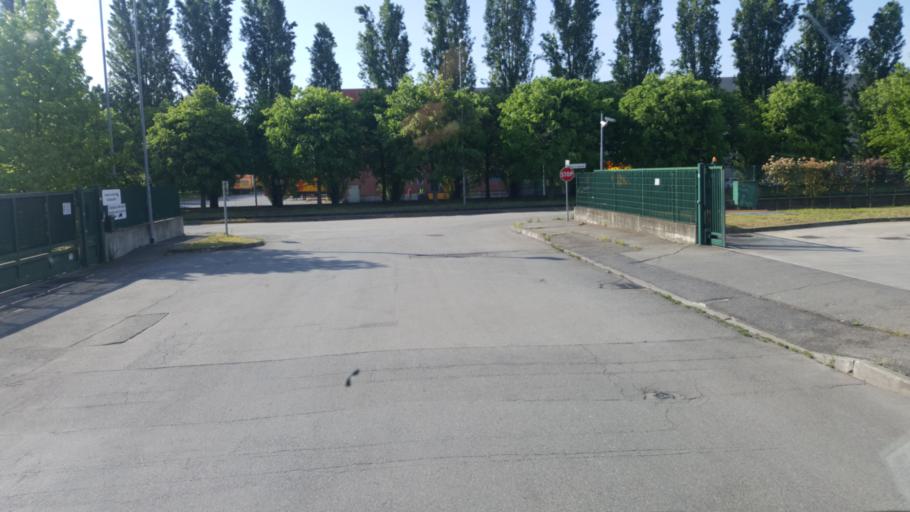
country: IT
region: Lombardy
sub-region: Citta metropolitana di Milano
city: Liscate
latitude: 45.4879
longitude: 9.4124
